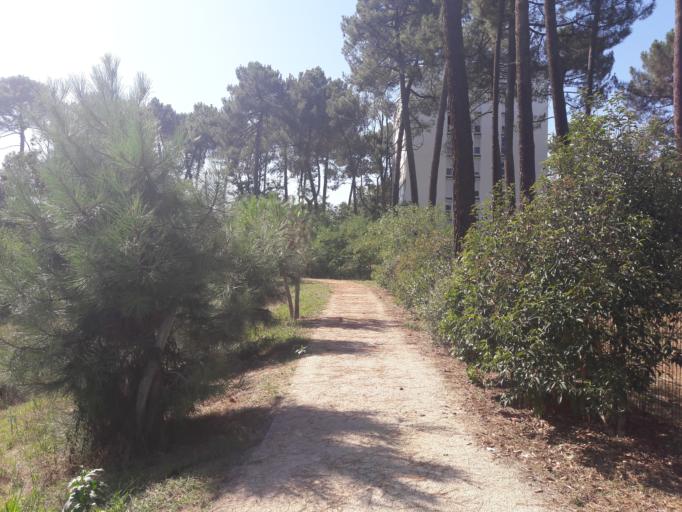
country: FR
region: Aquitaine
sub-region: Departement de la Gironde
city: Leognan
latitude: 44.7615
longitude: -0.5759
